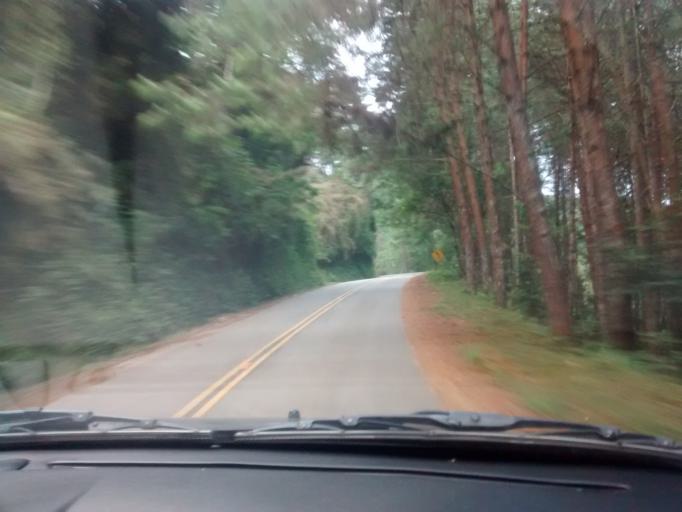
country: BR
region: Sao Paulo
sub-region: Campos Do Jordao
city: Campos do Jordao
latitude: -22.6508
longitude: -45.6236
